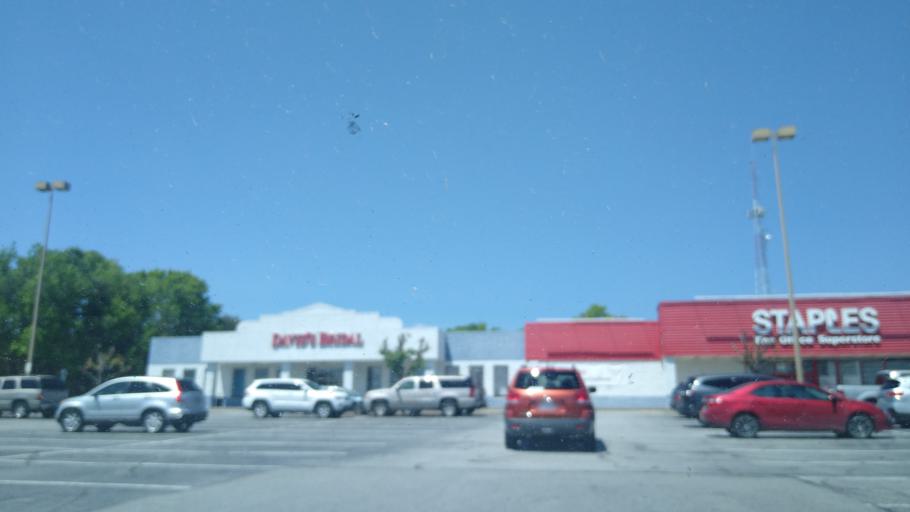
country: US
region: North Carolina
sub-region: Guilford County
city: Jamestown
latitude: 36.0585
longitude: -79.8881
